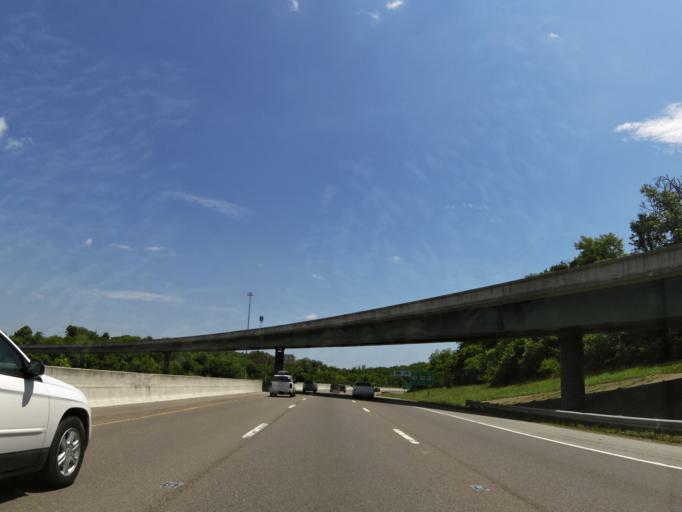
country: US
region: Tennessee
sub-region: Knox County
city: Knoxville
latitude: 36.0124
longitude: -83.8618
